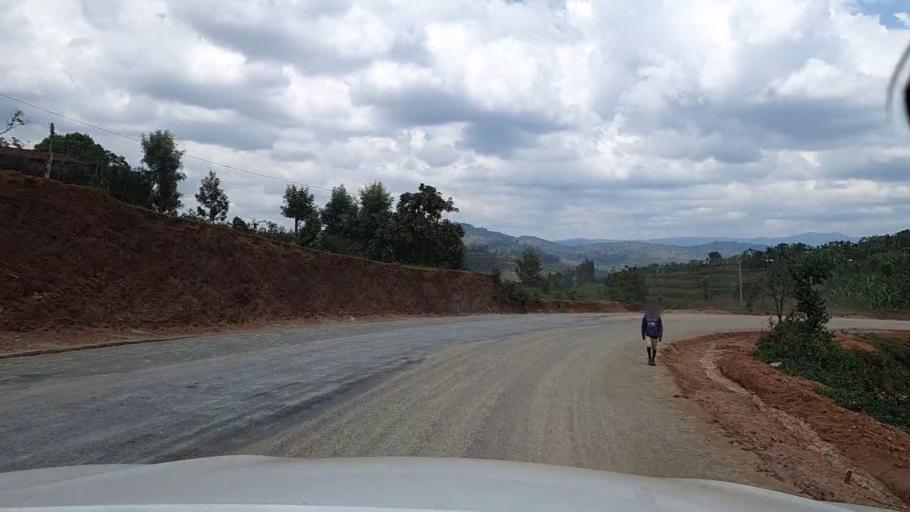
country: RW
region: Southern Province
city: Butare
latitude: -2.6986
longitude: 29.5631
